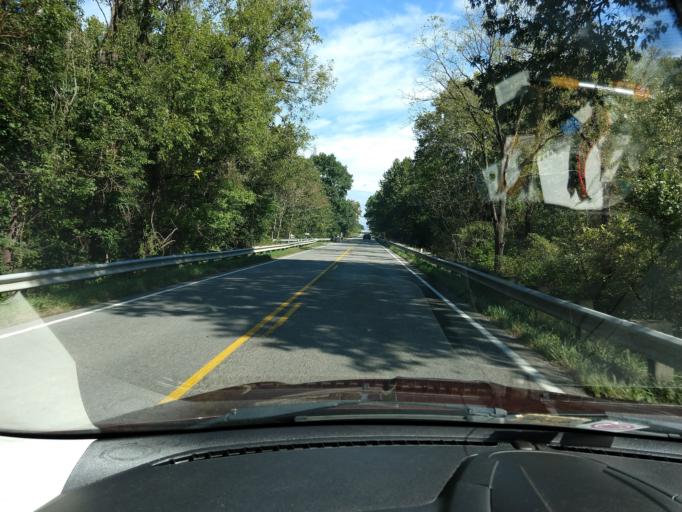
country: US
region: Virginia
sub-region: Augusta County
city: Crimora
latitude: 38.1849
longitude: -78.8419
